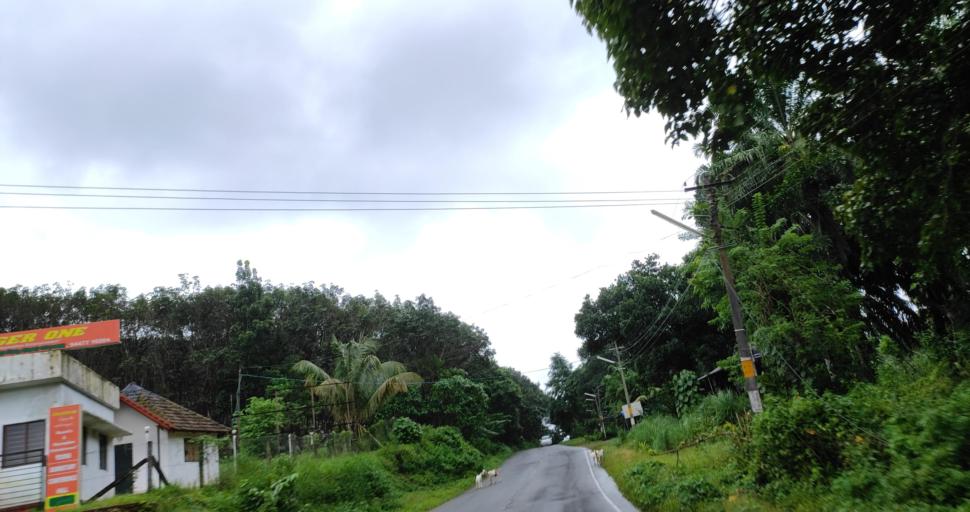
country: IN
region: Kerala
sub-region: Ernakulam
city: Angamali
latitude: 10.2919
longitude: 76.5404
